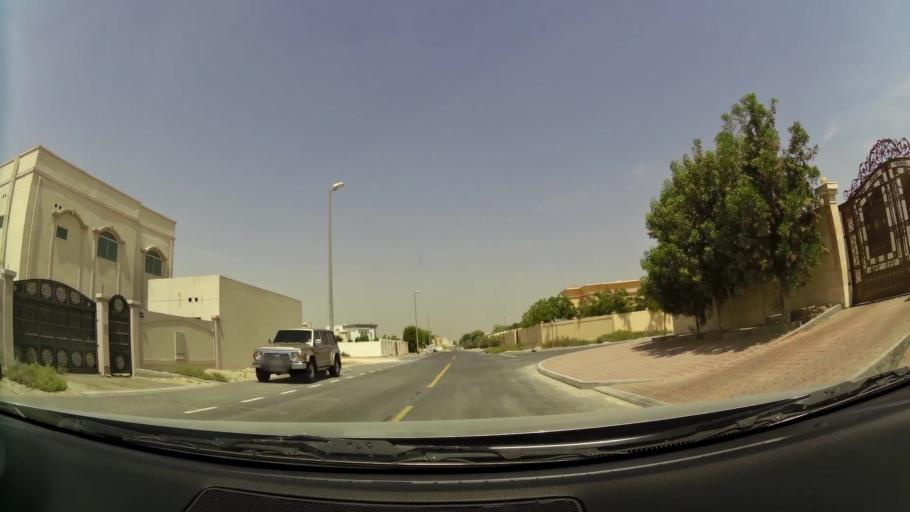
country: AE
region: Ash Shariqah
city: Sharjah
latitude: 25.1768
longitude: 55.4242
